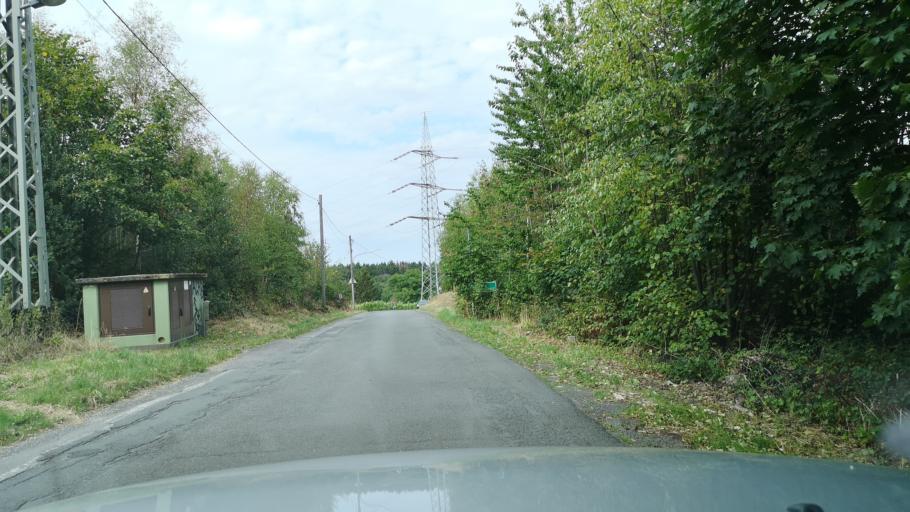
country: DE
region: North Rhine-Westphalia
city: Sprockhovel
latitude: 51.3498
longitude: 7.1950
